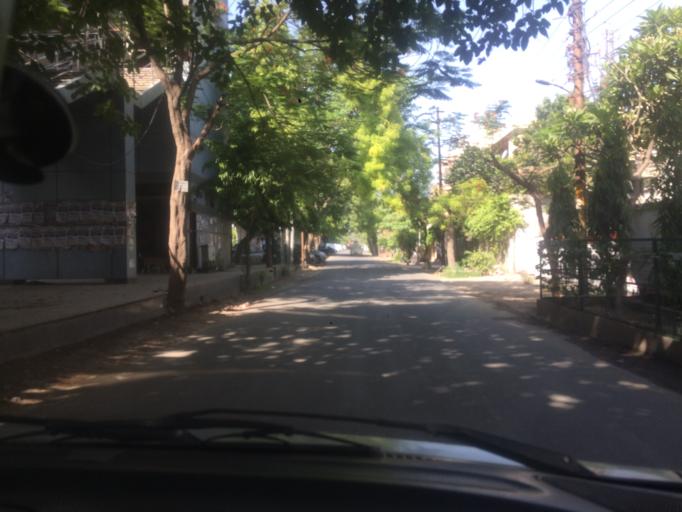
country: IN
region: Uttar Pradesh
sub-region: Gautam Buddha Nagar
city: Noida
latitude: 28.5773
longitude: 77.3367
